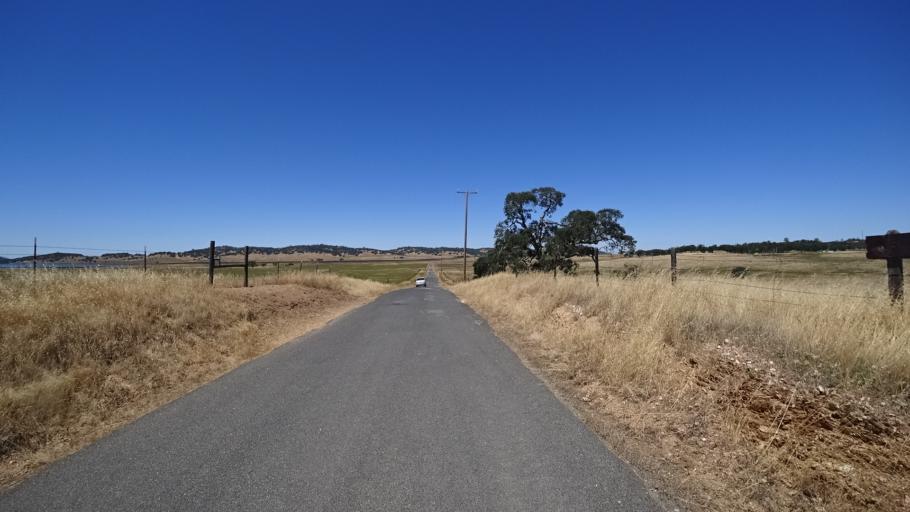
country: US
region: California
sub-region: Calaveras County
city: Copperopolis
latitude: 38.0538
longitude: -120.7442
